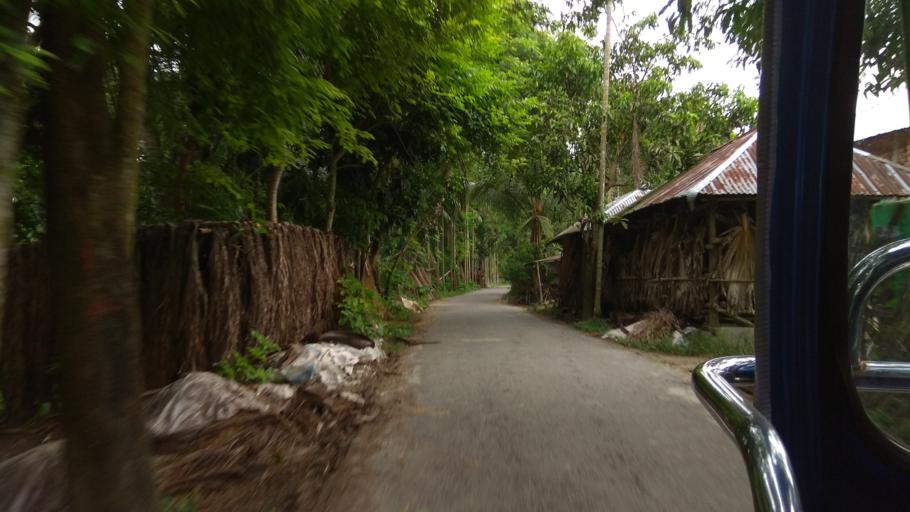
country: BD
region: Khulna
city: Kalia
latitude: 23.0355
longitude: 89.6566
